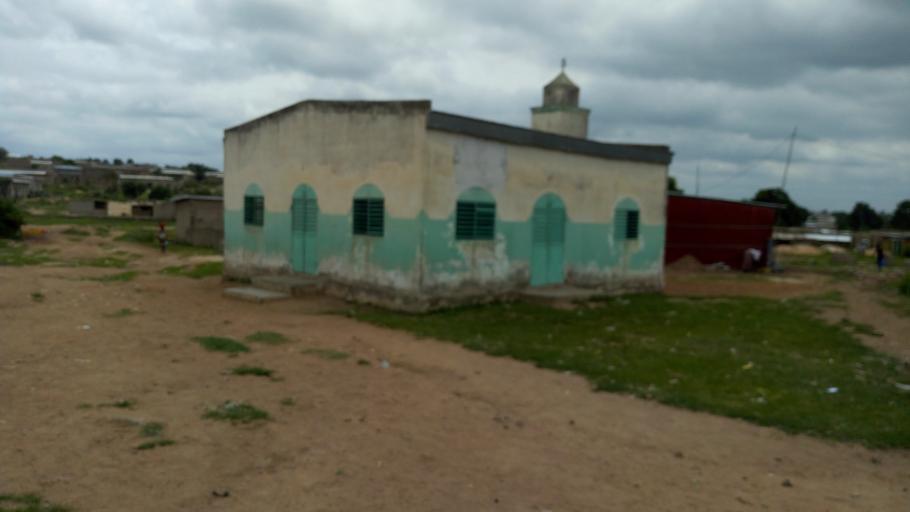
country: CI
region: Vallee du Bandama
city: Bouake
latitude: 7.7326
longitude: -5.0459
